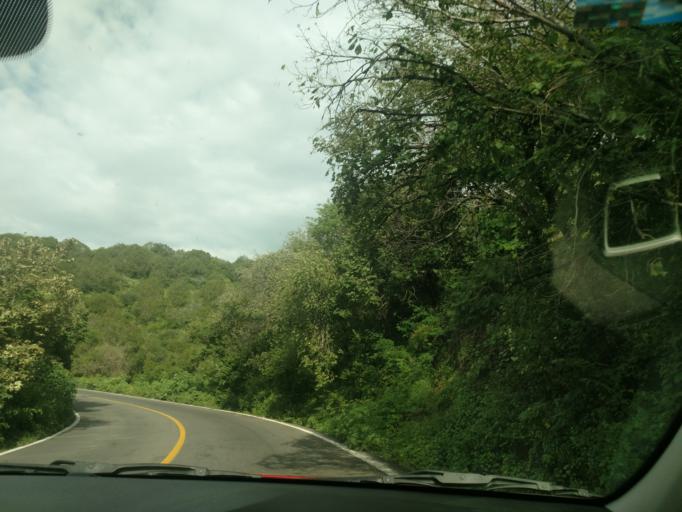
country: MX
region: Jalisco
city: Ameca
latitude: 20.5405
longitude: -104.1948
